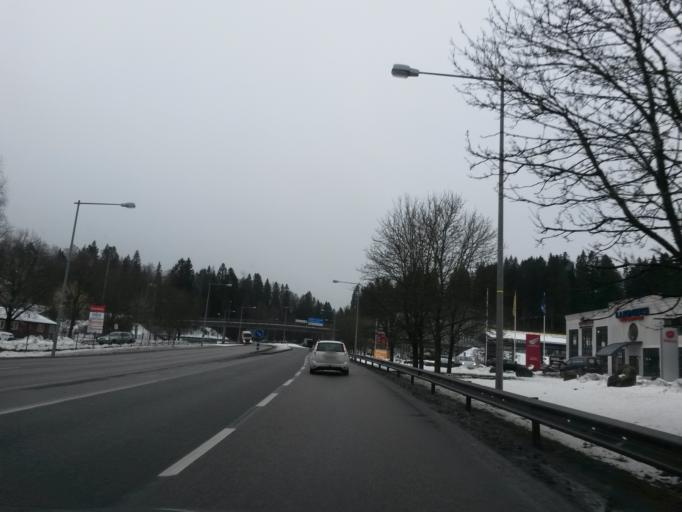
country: SE
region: Vaestra Goetaland
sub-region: Boras Kommun
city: Boras
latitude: 57.7058
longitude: 12.9496
